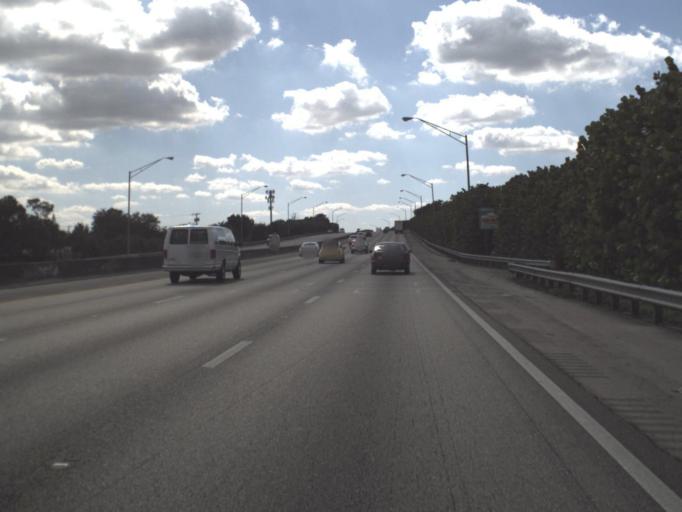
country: US
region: Florida
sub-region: Broward County
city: Pembroke Pines
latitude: 25.9987
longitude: -80.2210
